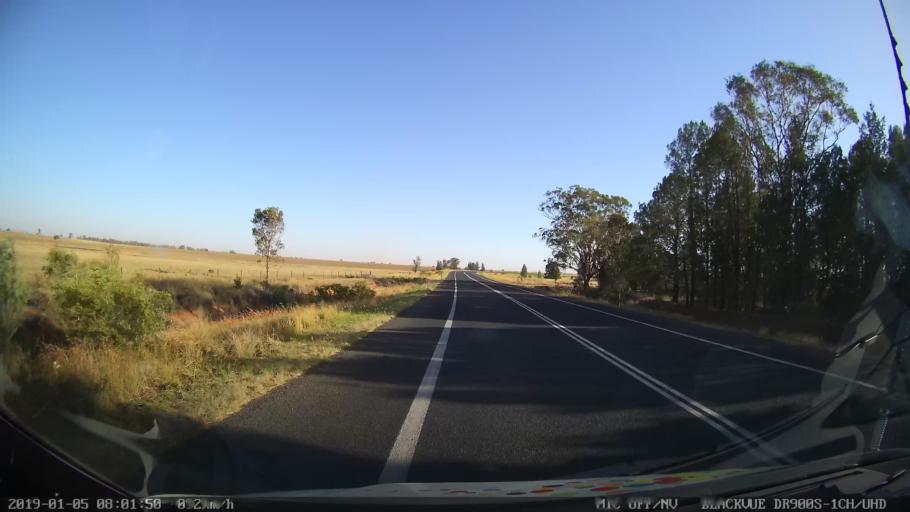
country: AU
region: New South Wales
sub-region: Gilgandra
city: Gilgandra
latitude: -31.6827
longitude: 148.7068
